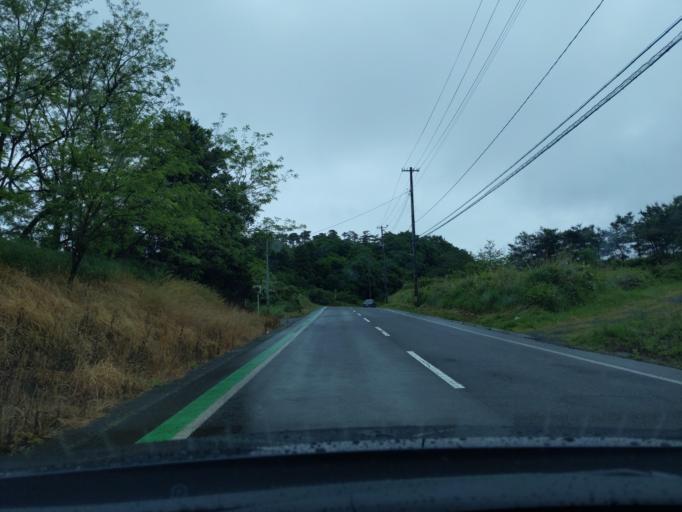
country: JP
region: Fukushima
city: Koriyama
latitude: 37.4291
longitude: 140.3030
